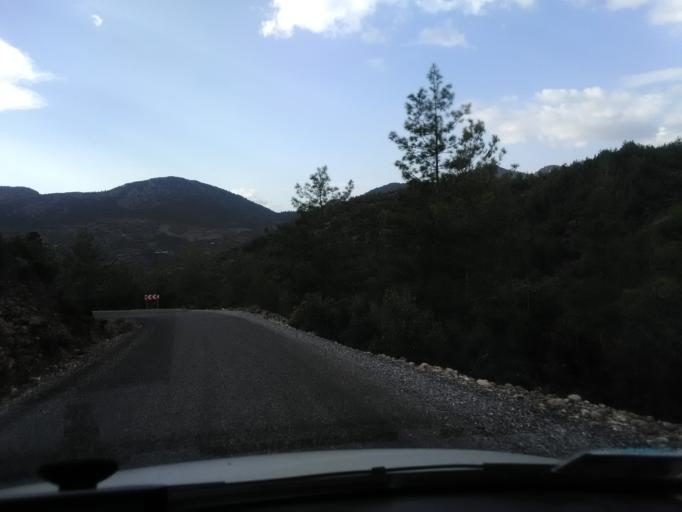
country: TR
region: Antalya
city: Gazipasa
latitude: 36.3053
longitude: 32.3955
